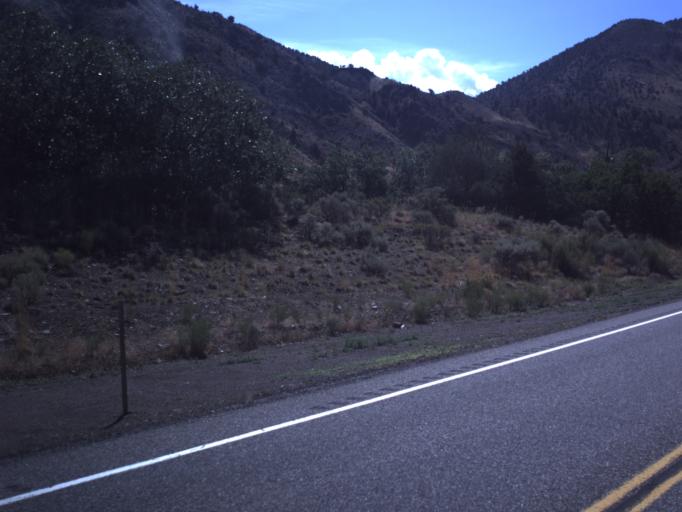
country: US
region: Utah
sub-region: Sevier County
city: Monroe
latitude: 38.5283
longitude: -112.2694
